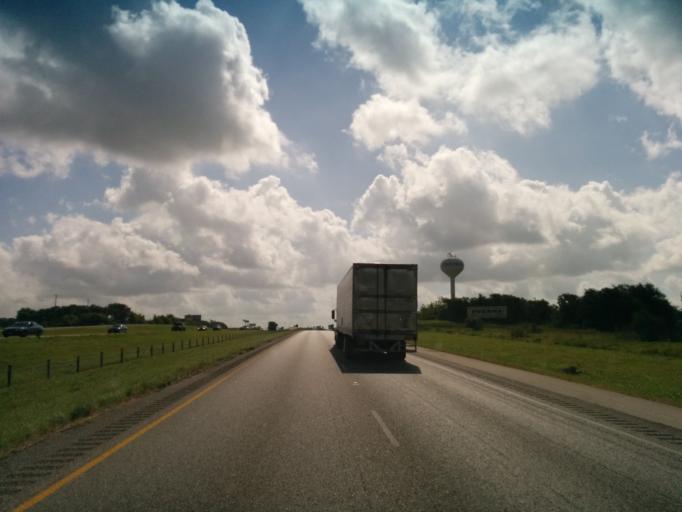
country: US
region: Texas
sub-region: Fayette County
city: Schulenburg
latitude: 29.6917
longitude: -96.9133
